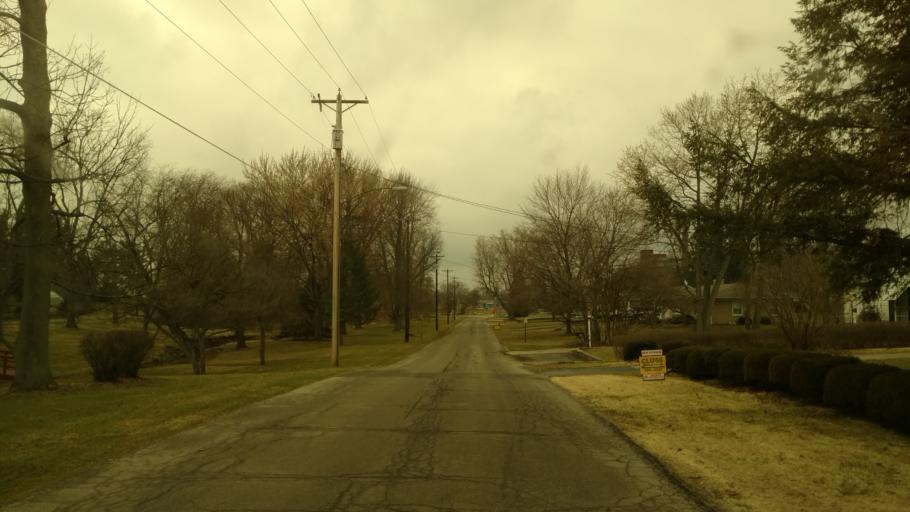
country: US
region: Ohio
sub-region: Richland County
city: Shelby
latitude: 40.8787
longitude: -82.6512
